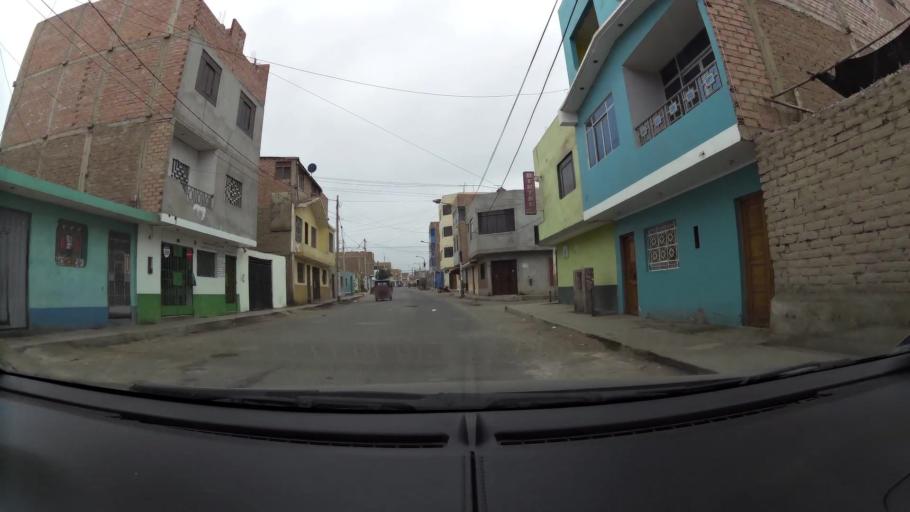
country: PE
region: Lima
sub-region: Barranca
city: Barranca
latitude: -10.7473
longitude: -77.7553
